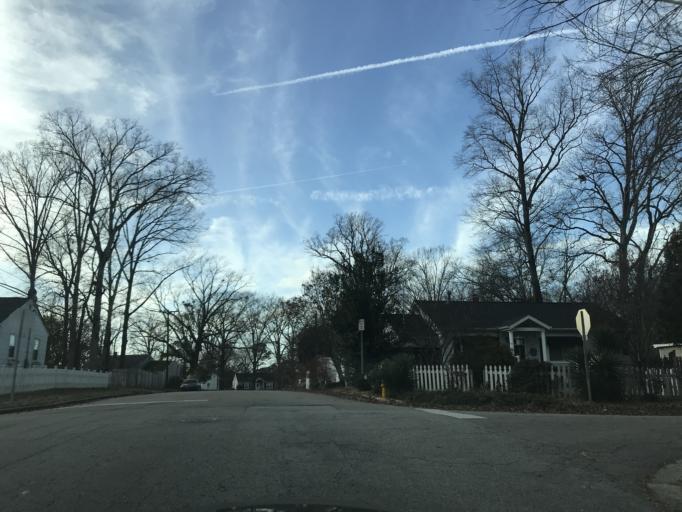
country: US
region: North Carolina
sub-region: Wake County
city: Raleigh
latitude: 35.7986
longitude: -78.6162
